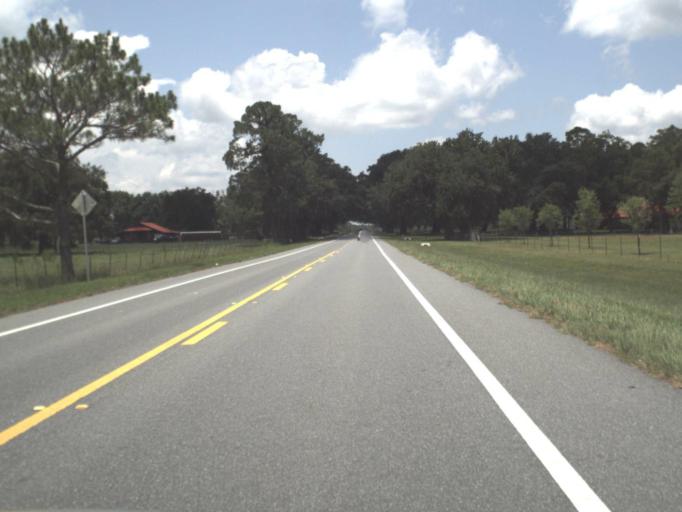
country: US
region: Florida
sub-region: Union County
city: Lake Butler
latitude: 30.0193
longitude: -82.4091
